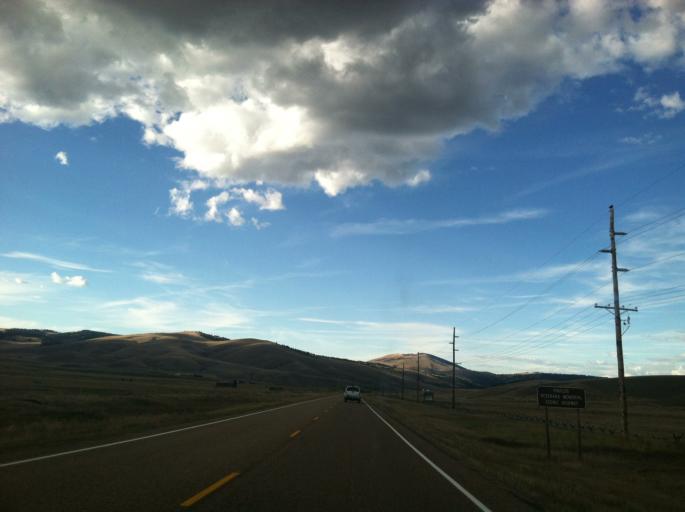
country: US
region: Montana
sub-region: Granite County
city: Philipsburg
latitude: 46.3522
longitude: -113.3139
